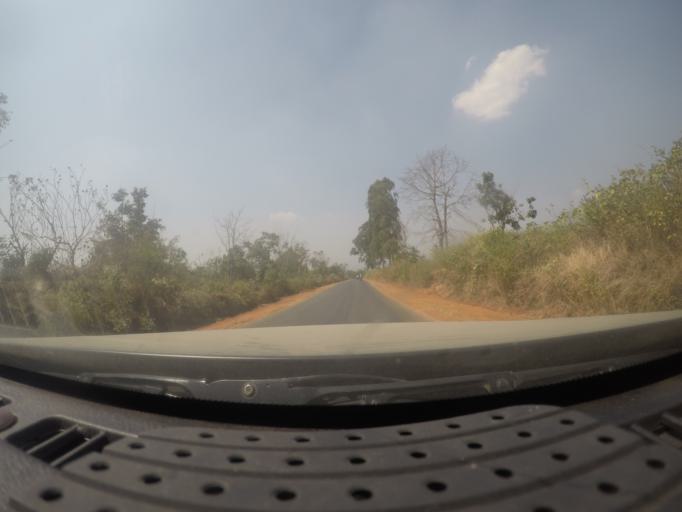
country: MM
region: Shan
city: Taunggyi
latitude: 21.0273
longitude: 96.5220
